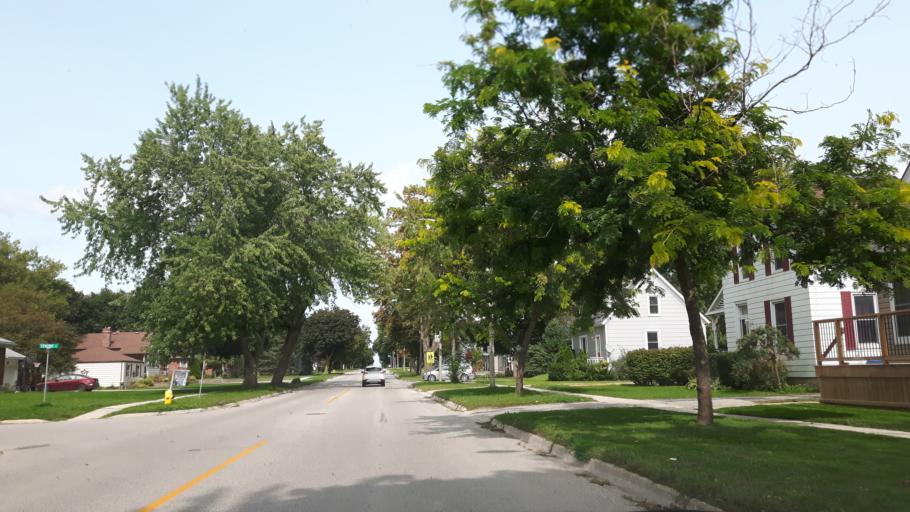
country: CA
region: Ontario
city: Huron East
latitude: 43.5552
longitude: -81.3918
